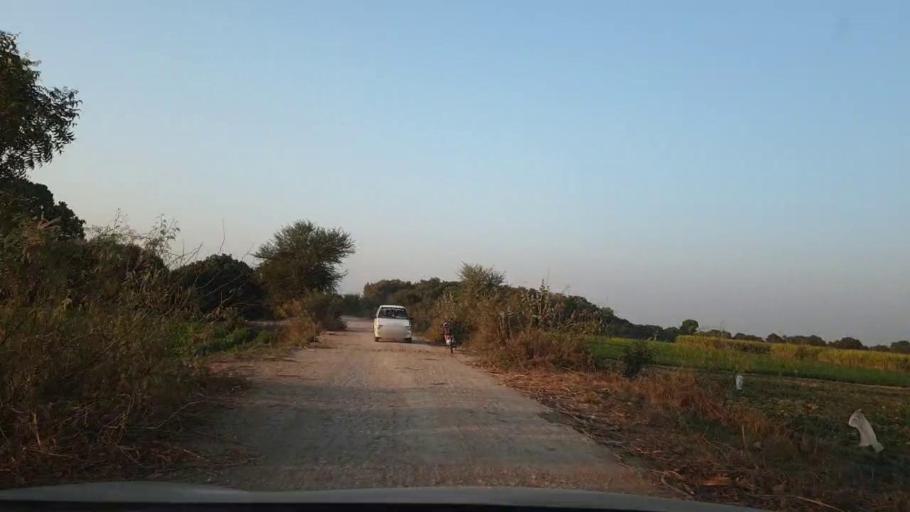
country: PK
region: Sindh
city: Tando Allahyar
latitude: 25.5086
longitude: 68.7411
